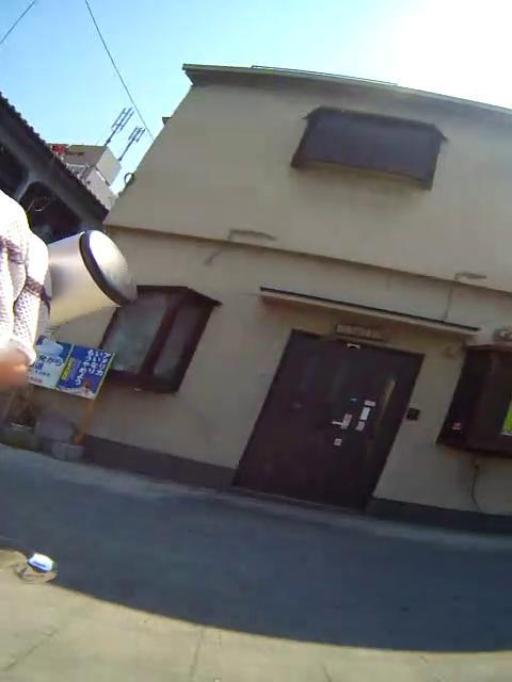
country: JP
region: Osaka
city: Yao
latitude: 34.6251
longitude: 135.5490
